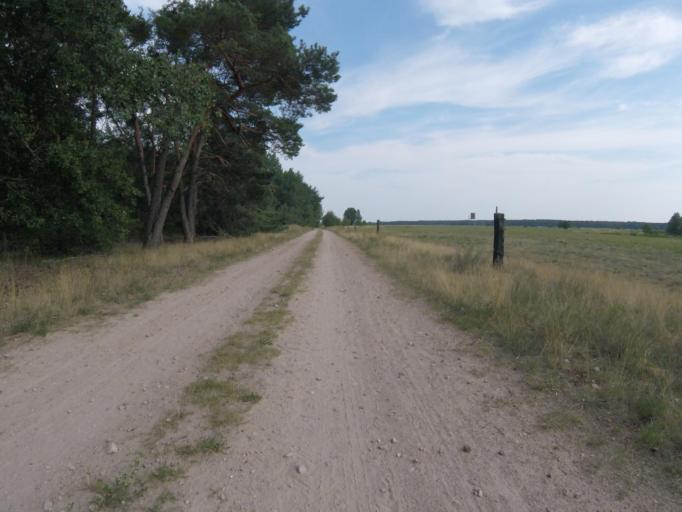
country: DE
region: Brandenburg
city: Spreenhagen
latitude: 52.2932
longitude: 13.8031
